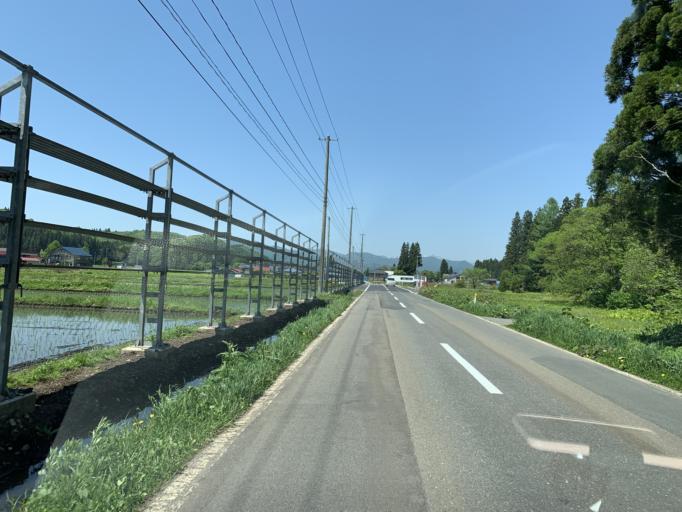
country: JP
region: Akita
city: Yokotemachi
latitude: 39.3786
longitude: 140.7598
